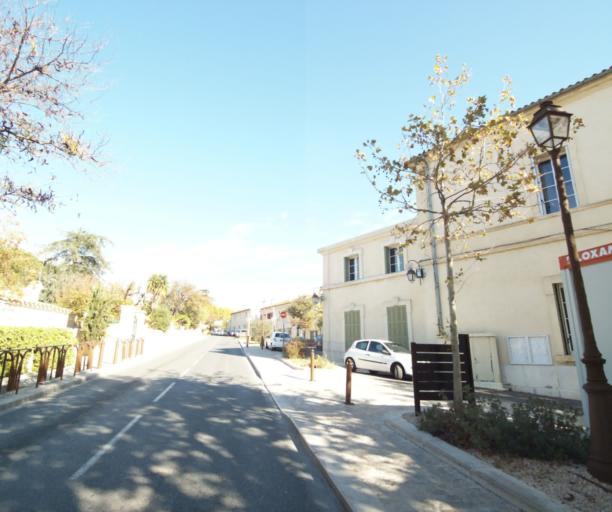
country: FR
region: Provence-Alpes-Cote d'Azur
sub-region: Departement des Bouches-du-Rhone
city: Ceyreste
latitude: 43.2143
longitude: 5.6315
